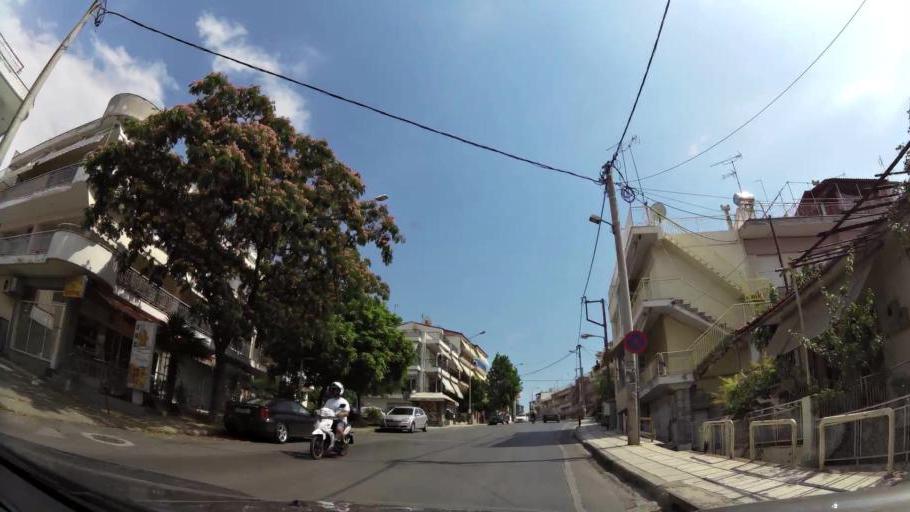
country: GR
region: Central Macedonia
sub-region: Nomos Thessalonikis
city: Polichni
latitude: 40.6652
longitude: 22.9469
